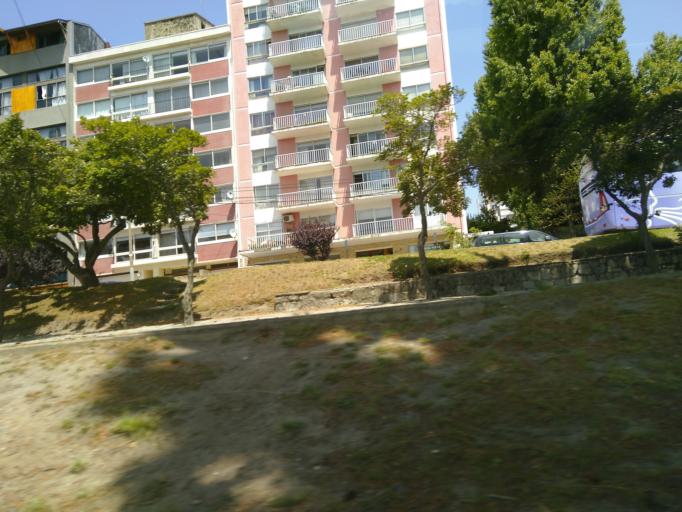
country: AR
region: Rio Negro
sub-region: Departamento de Bariloche
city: San Carlos de Bariloche
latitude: -41.1327
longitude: -71.3058
